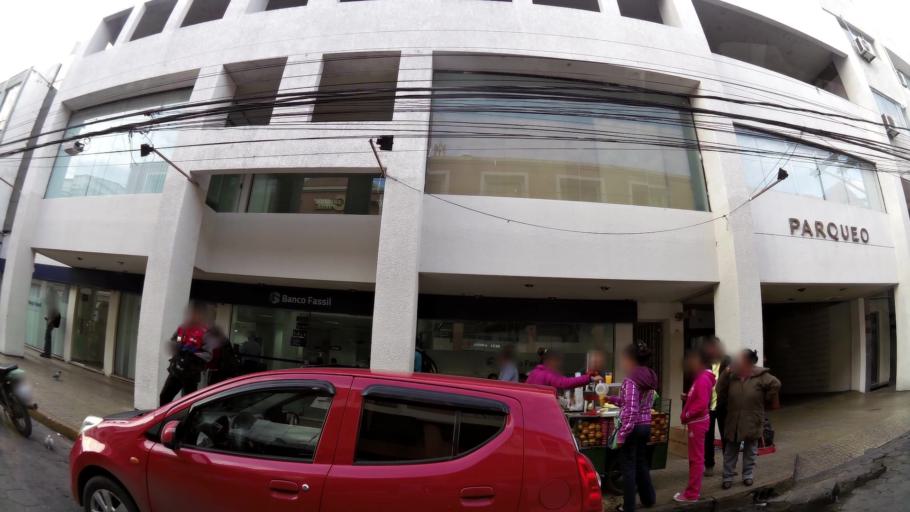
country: BO
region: Santa Cruz
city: Santa Cruz de la Sierra
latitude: -17.7827
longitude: -63.1808
